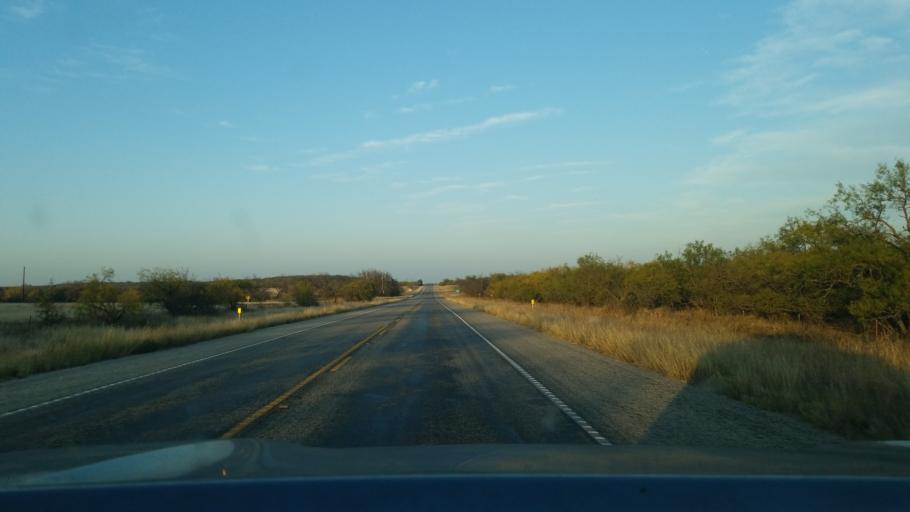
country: US
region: Texas
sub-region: Eastland County
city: Cisco
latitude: 32.4328
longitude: -98.9248
